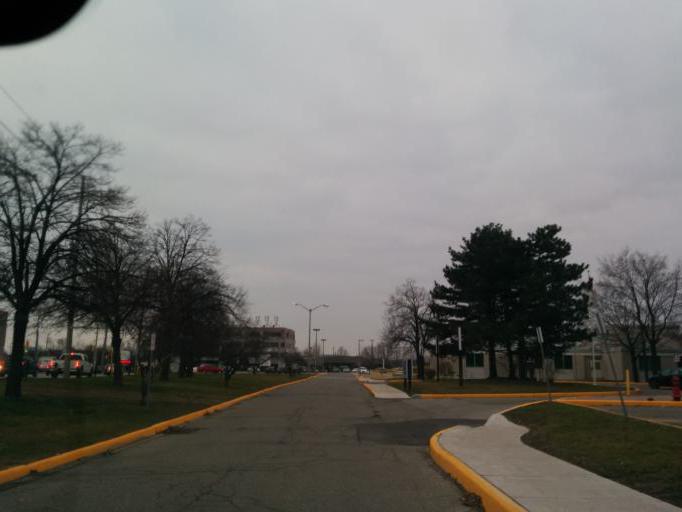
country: CA
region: Ontario
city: Etobicoke
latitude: 43.6105
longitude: -79.5617
